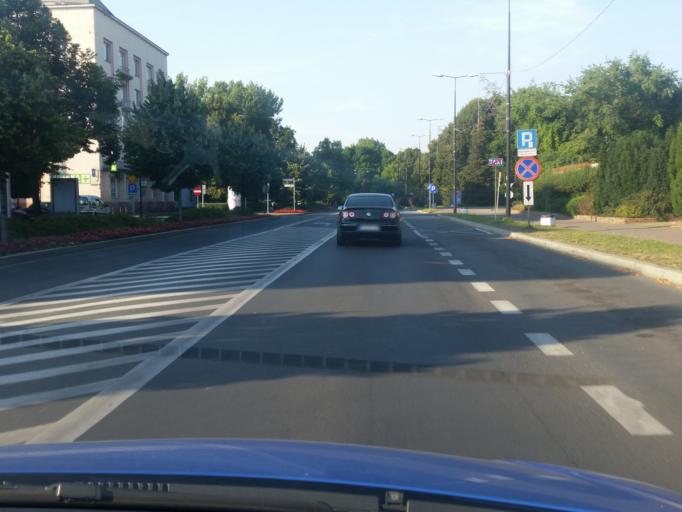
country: PL
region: Silesian Voivodeship
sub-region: Sosnowiec
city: Sosnowiec
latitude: 50.2778
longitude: 19.1342
